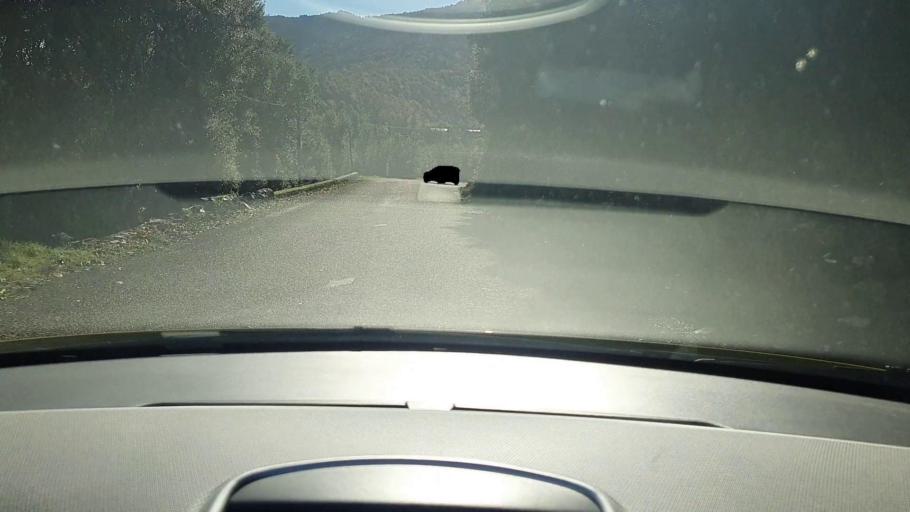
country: FR
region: Languedoc-Roussillon
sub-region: Departement du Gard
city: Valleraugue
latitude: 44.1714
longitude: 3.6541
